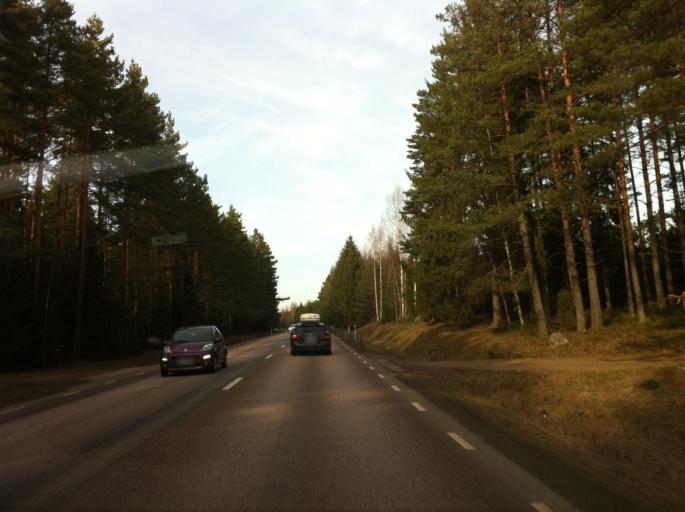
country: SE
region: Vaestra Goetaland
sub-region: Gullspangs Kommun
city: Gullspang
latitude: 59.0719
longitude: 14.1551
